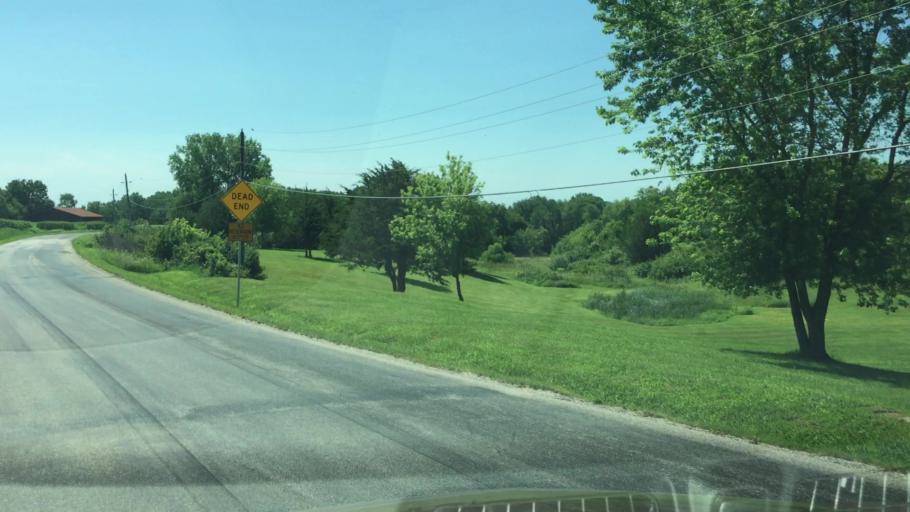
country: US
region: Iowa
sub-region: Linn County
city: Ely
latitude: 41.8148
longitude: -91.6162
